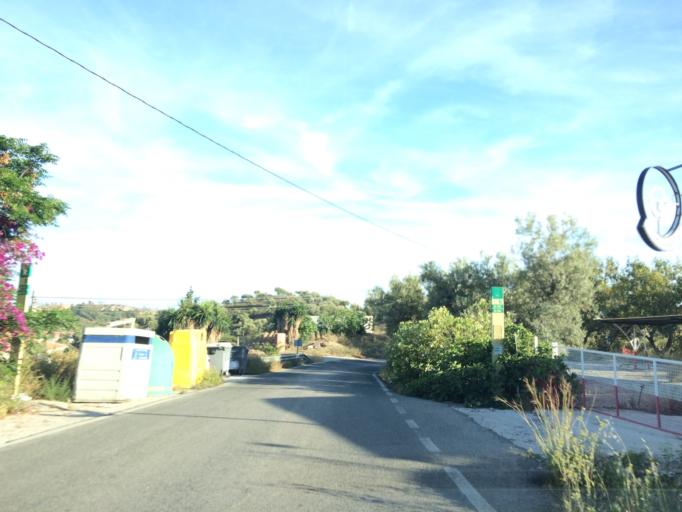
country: ES
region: Andalusia
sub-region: Provincia de Malaga
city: Totalan
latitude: 36.7310
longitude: -4.3399
